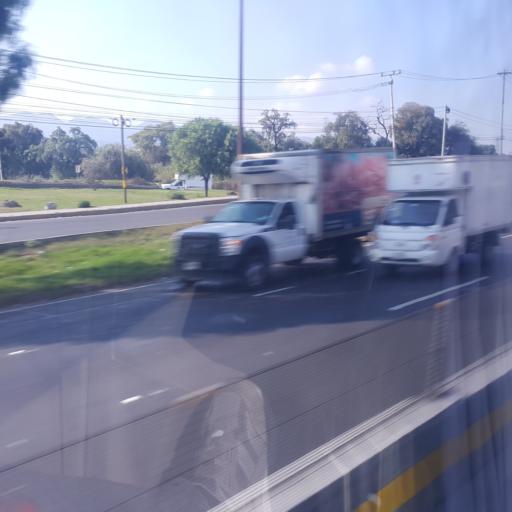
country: MX
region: Mexico
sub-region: Cuautitlan
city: San Jose del Puente
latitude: 19.7025
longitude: -99.2053
